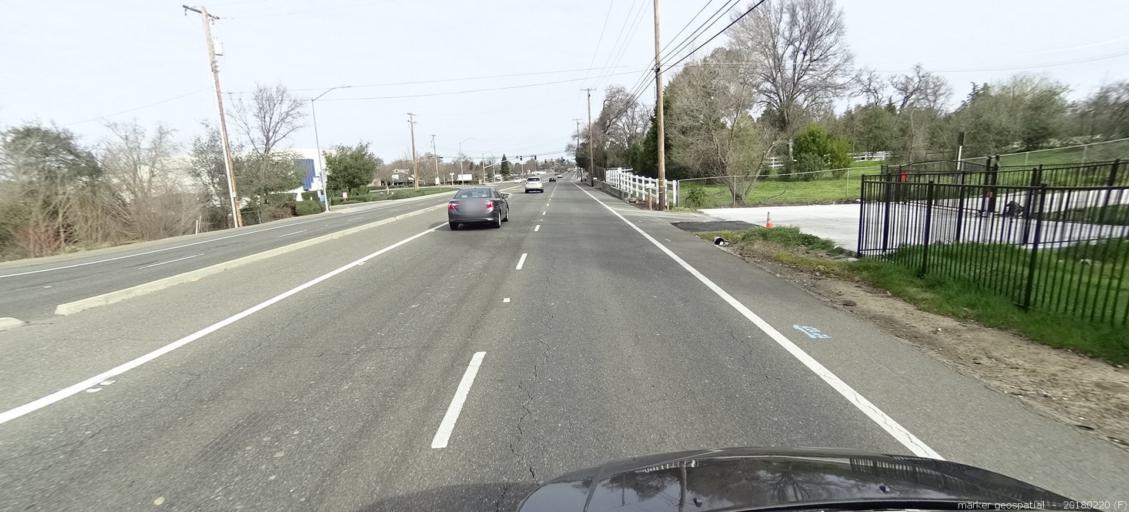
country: US
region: California
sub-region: Sacramento County
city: Orangevale
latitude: 38.7060
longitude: -121.2252
